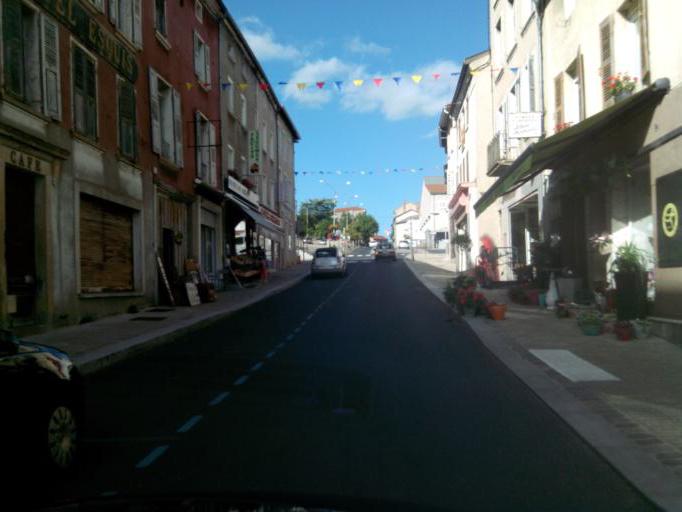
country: FR
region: Auvergne
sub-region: Departement de la Haute-Loire
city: Craponne-sur-Arzon
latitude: 45.3320
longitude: 3.8476
